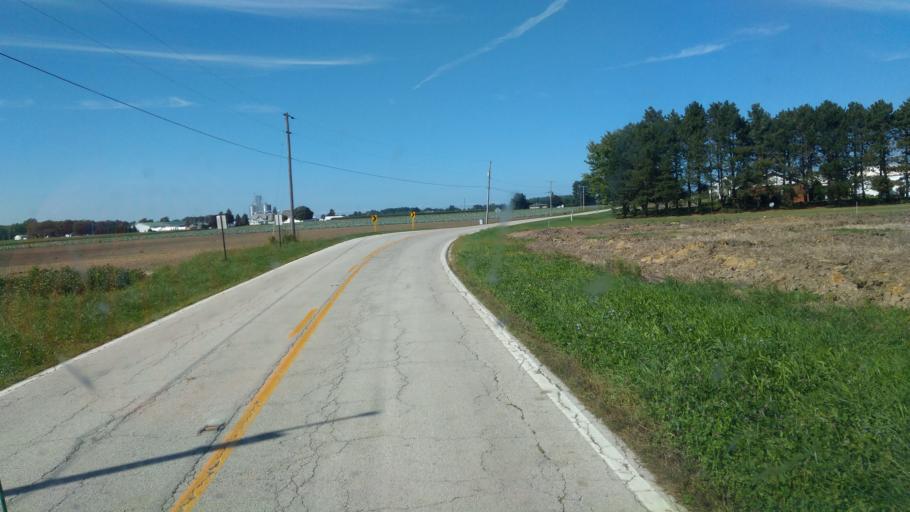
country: US
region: Ohio
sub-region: Ottawa County
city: Port Clinton
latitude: 41.4106
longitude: -82.8939
